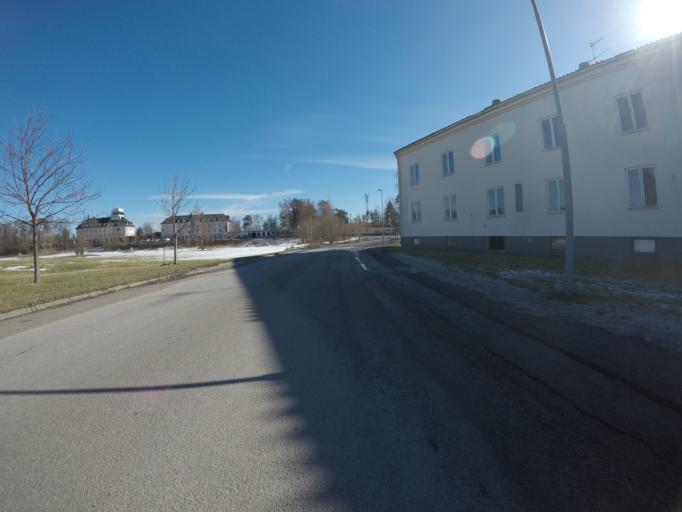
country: SE
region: Vaestmanland
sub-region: Vasteras
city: Vasteras
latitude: 59.5877
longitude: 16.6202
